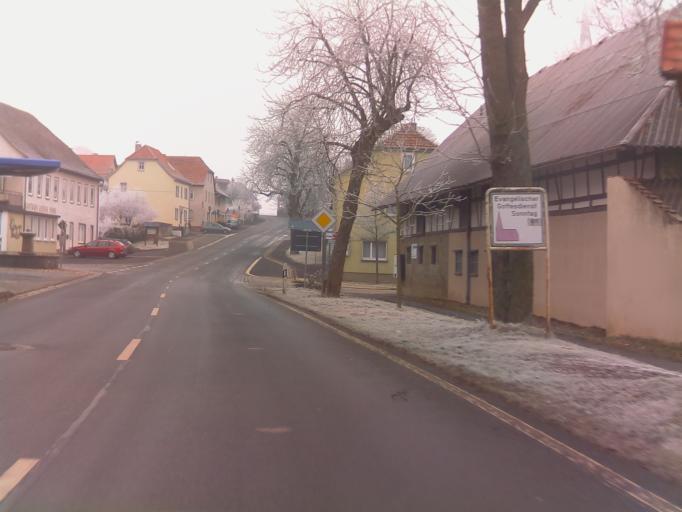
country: DE
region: Bavaria
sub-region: Regierungsbezirk Unterfranken
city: Sondheim vor der Rhoen
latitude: 50.4654
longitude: 10.1592
